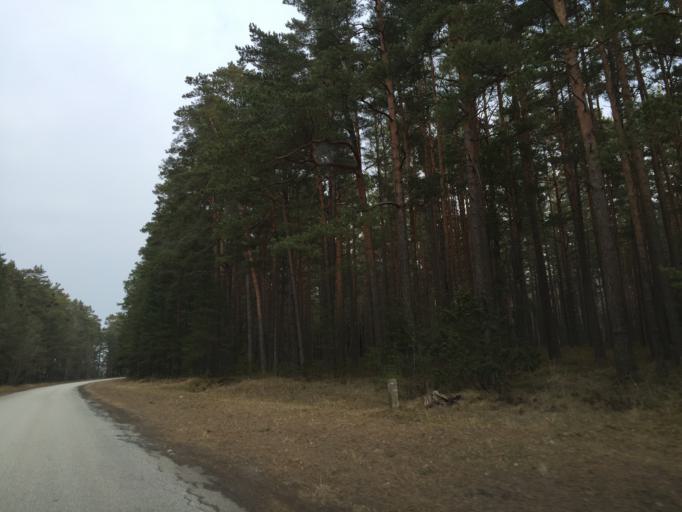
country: LV
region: Salacgrivas
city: Ainazi
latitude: 57.9475
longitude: 24.3914
